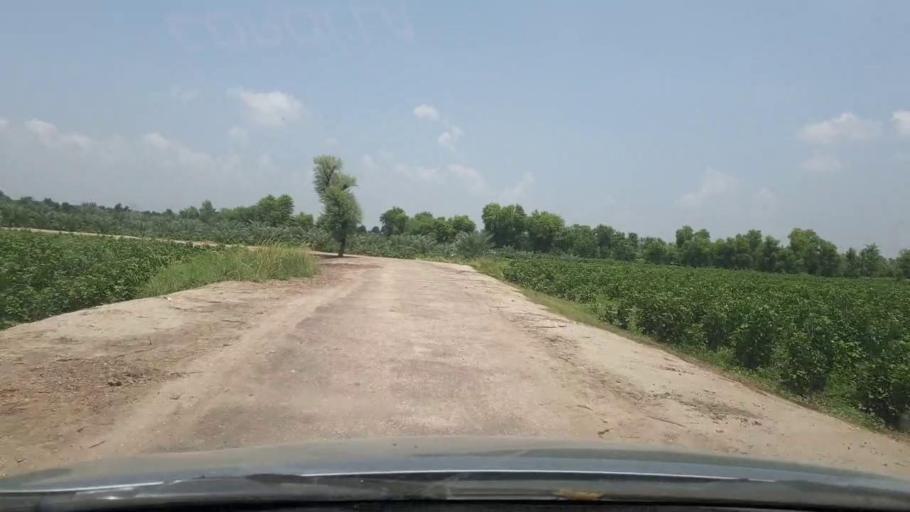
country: PK
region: Sindh
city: Khairpur
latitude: 27.4738
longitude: 68.7319
